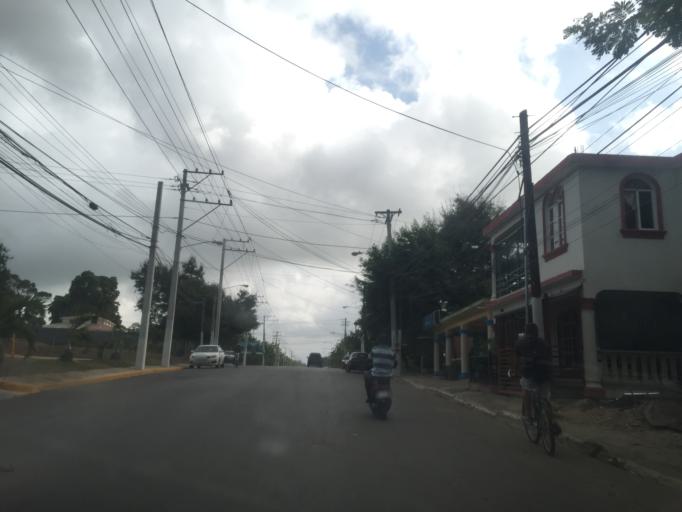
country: DO
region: Santiago
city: Santiago de los Caballeros
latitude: 19.4121
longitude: -70.7180
